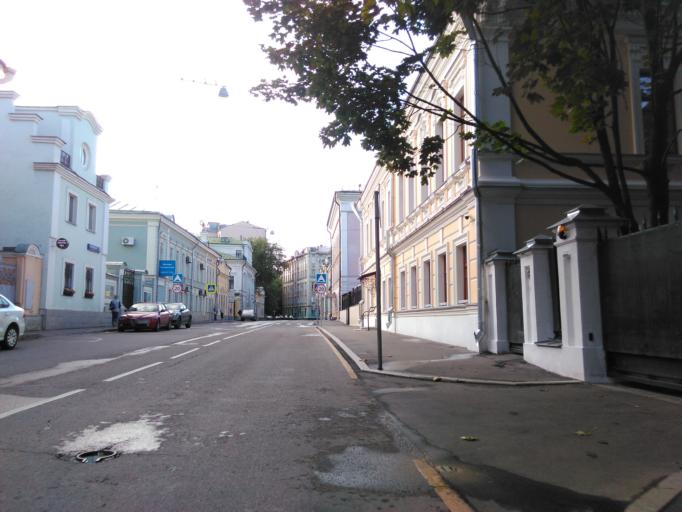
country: RU
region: Moscow
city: Taganskiy
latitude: 55.7548
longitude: 37.6542
